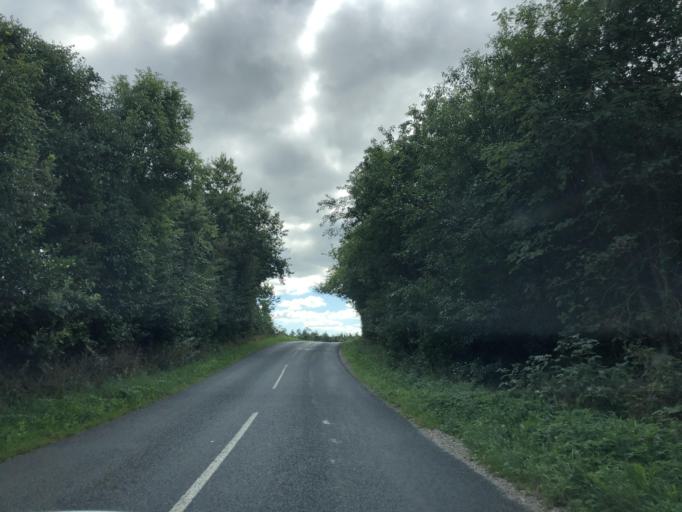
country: DK
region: North Denmark
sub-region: Vesthimmerland Kommune
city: Alestrup
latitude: 56.5994
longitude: 9.4325
